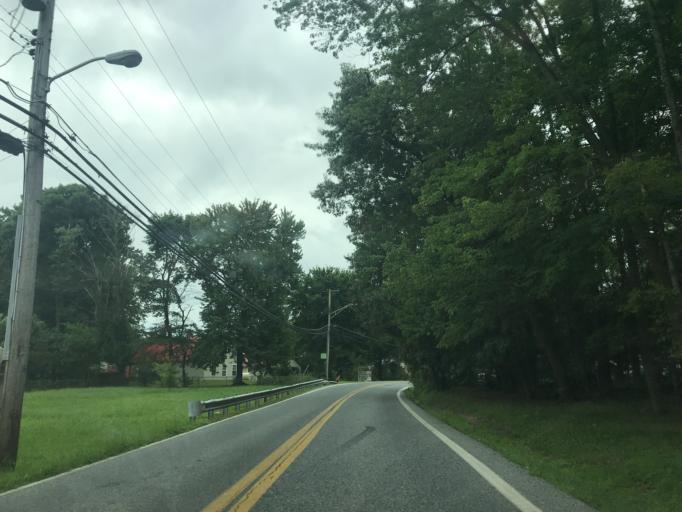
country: US
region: Maryland
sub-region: Baltimore County
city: Essex
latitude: 39.2912
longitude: -76.4406
